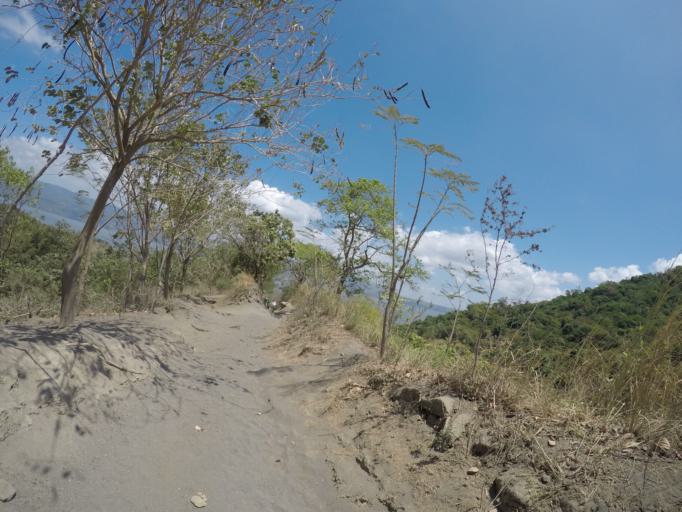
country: PH
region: Calabarzon
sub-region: Province of Batangas
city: Bugaan
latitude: 14.0286
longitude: 121.0011
